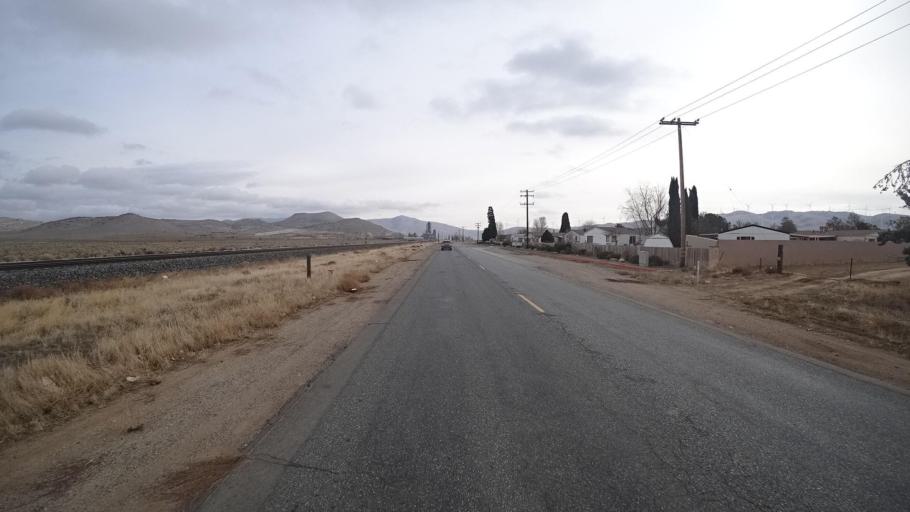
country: US
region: California
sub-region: Kern County
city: Tehachapi
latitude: 35.1243
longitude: -118.3902
